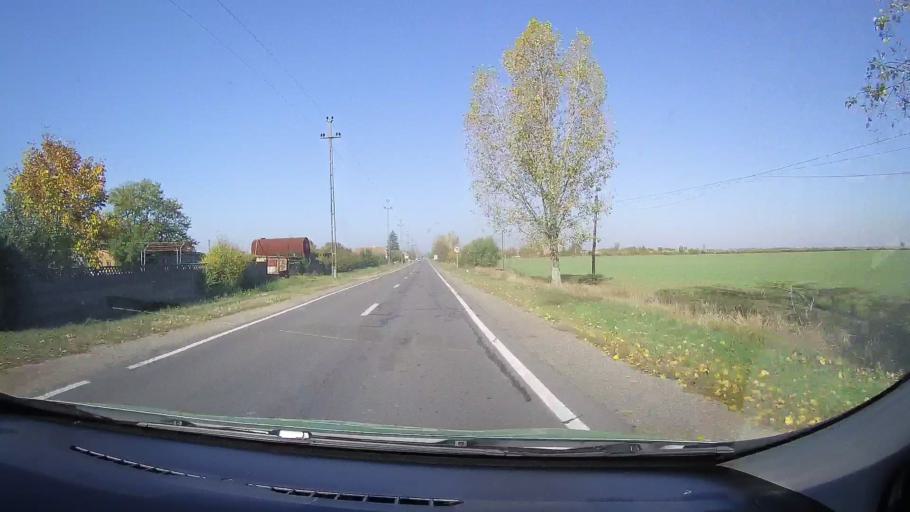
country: RO
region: Satu Mare
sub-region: Comuna Urziceni
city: Urziceni
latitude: 47.7242
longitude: 22.4123
